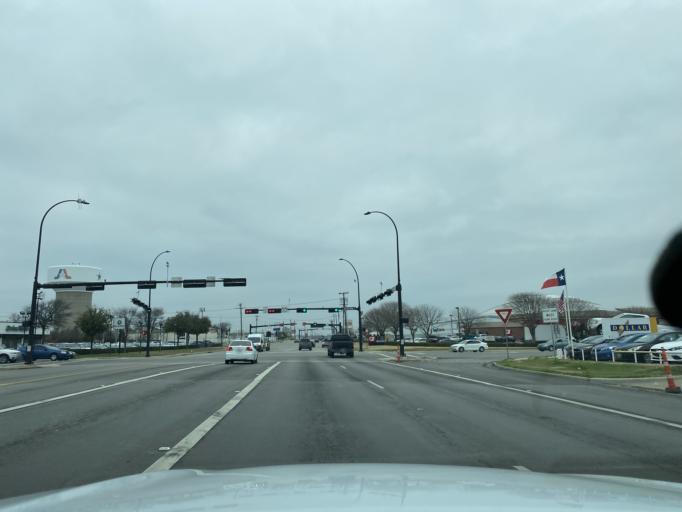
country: US
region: Texas
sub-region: Tarrant County
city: Arlington
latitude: 32.7385
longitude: -97.0973
